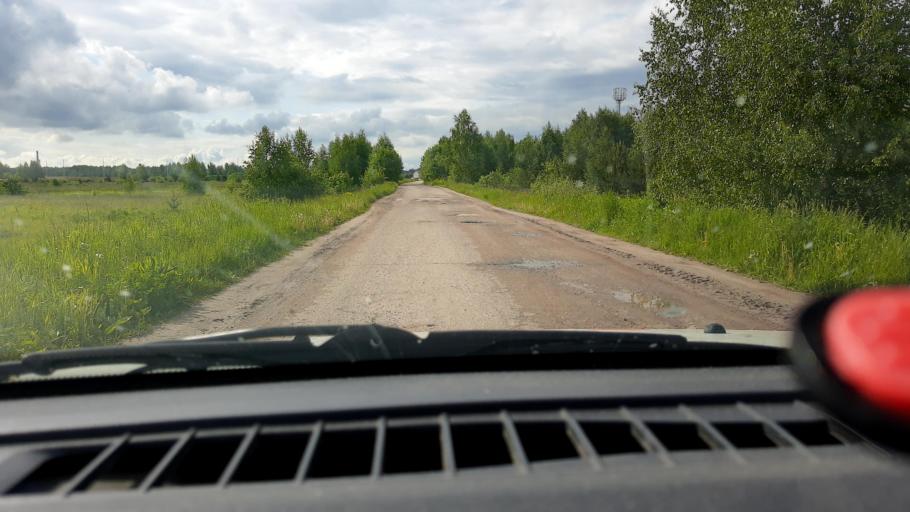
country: RU
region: Nizjnij Novgorod
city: Neklyudovo
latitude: 56.4312
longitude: 43.9607
